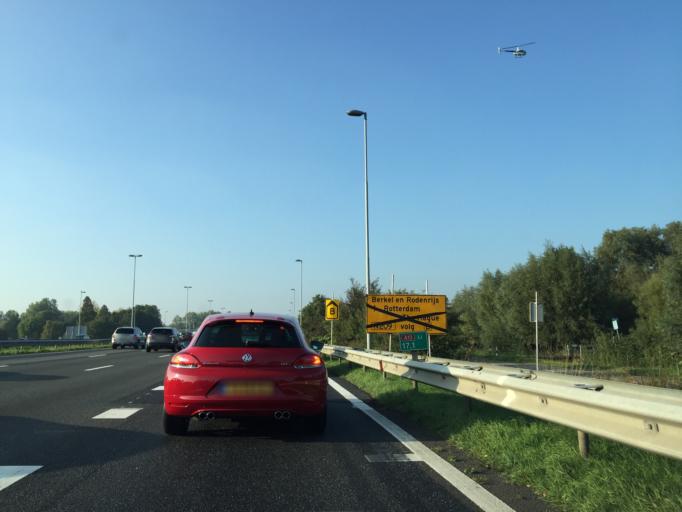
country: NL
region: South Holland
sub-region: Gemeente Schiedam
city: Schiedam
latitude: 51.9472
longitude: 4.4205
